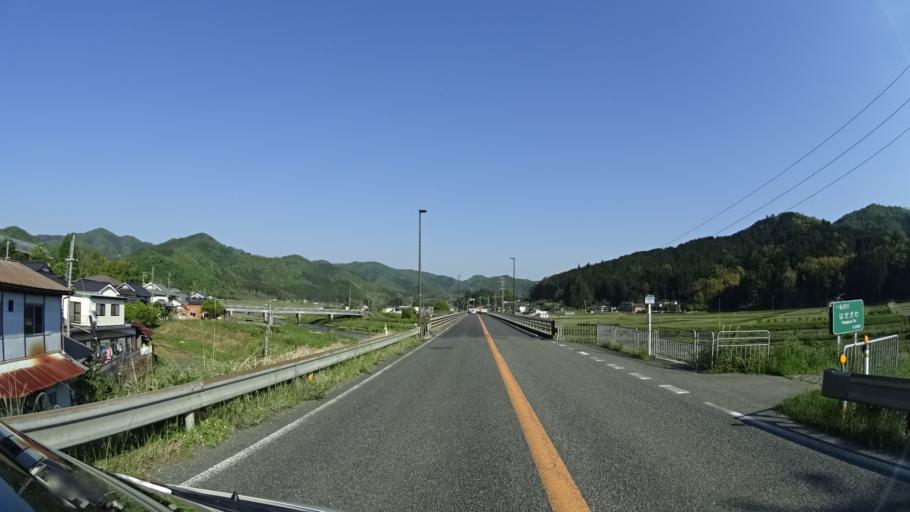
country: JP
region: Kyoto
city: Ayabe
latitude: 35.2521
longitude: 135.2080
